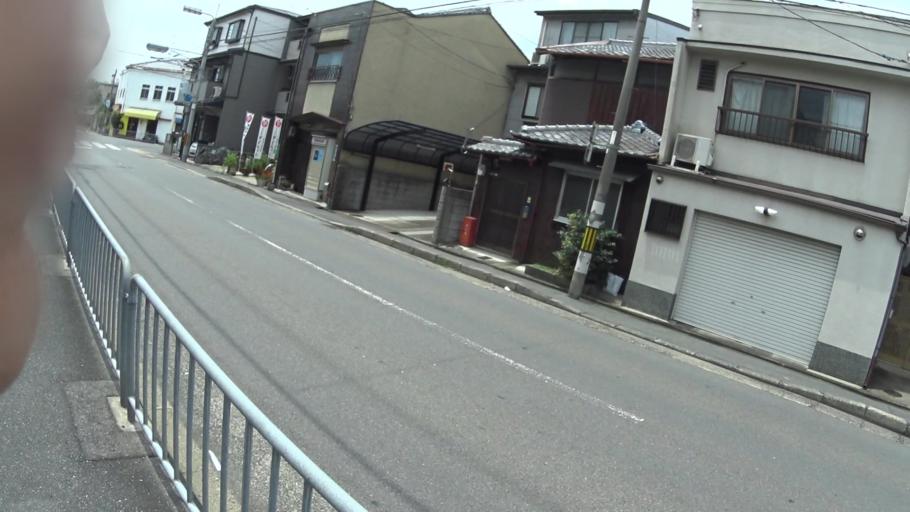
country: JP
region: Kyoto
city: Kyoto
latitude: 34.9823
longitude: 135.7462
